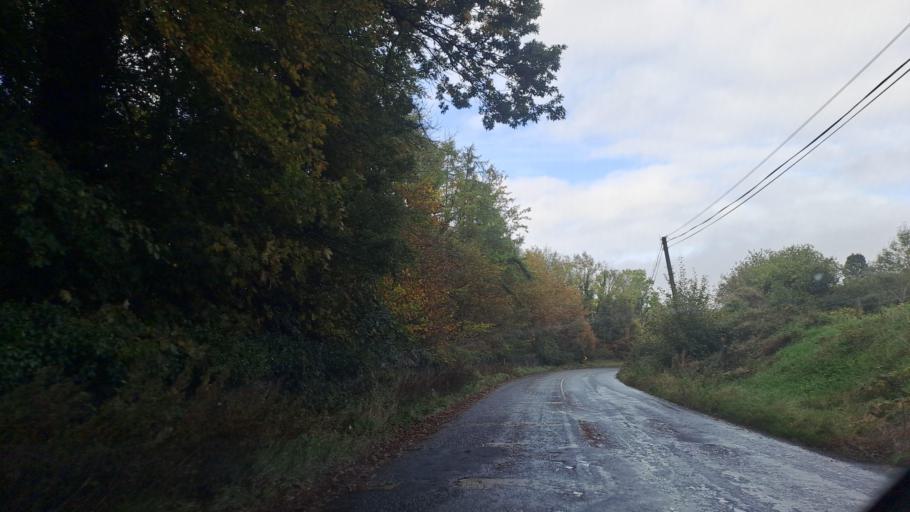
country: IE
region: Ulster
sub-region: County Monaghan
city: Carrickmacross
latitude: 53.9499
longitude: -6.7178
